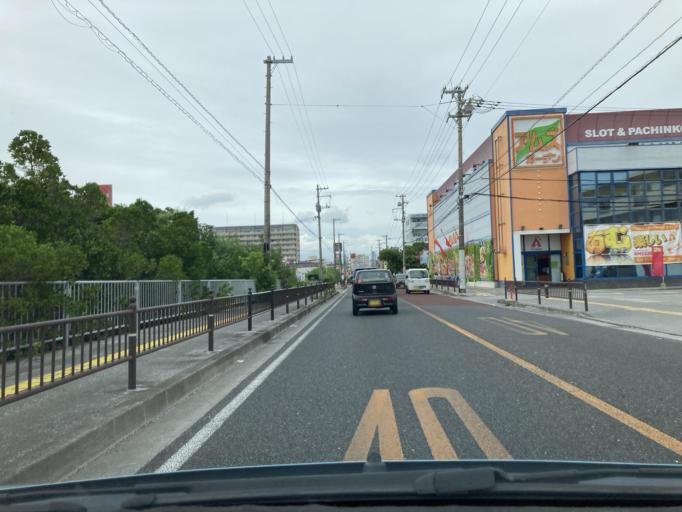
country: JP
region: Okinawa
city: Itoman
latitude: 26.1381
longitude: 127.6707
